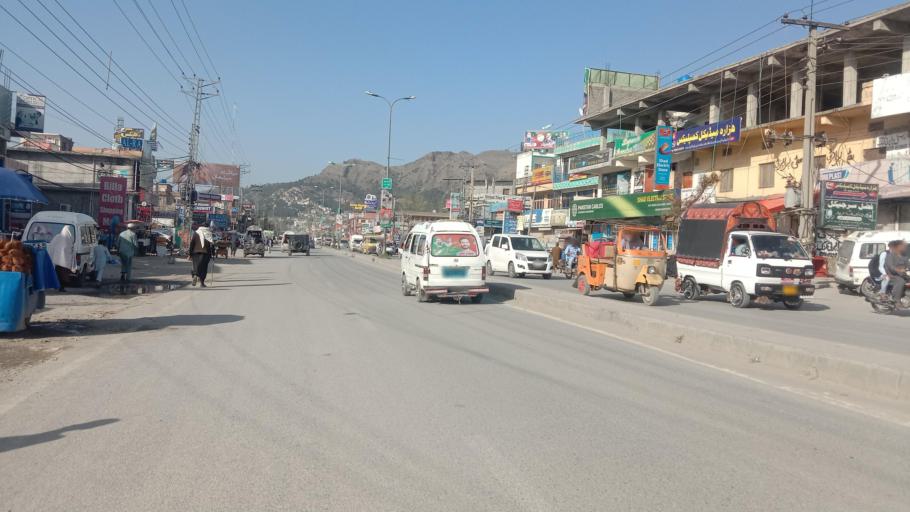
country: PK
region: Khyber Pakhtunkhwa
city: Abbottabad
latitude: 34.1968
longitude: 73.2366
